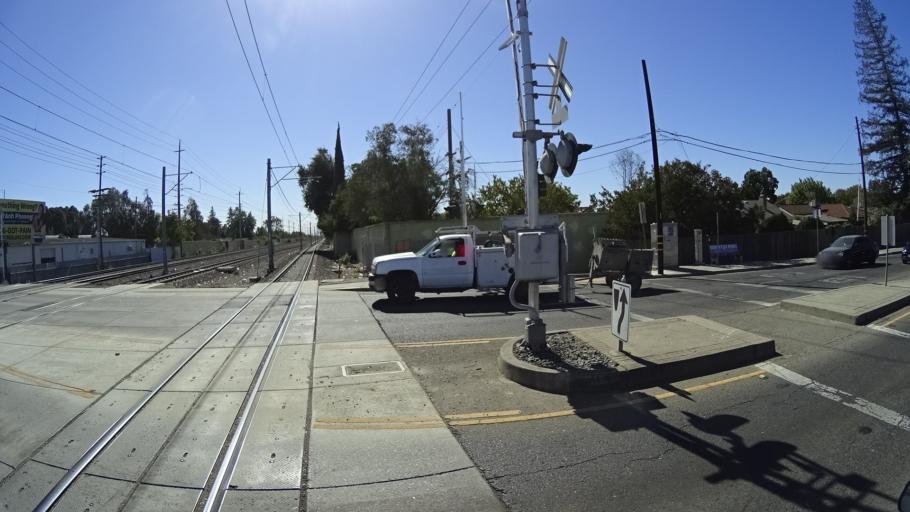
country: US
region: California
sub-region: Sacramento County
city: Parkway
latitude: 38.5241
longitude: -121.4793
